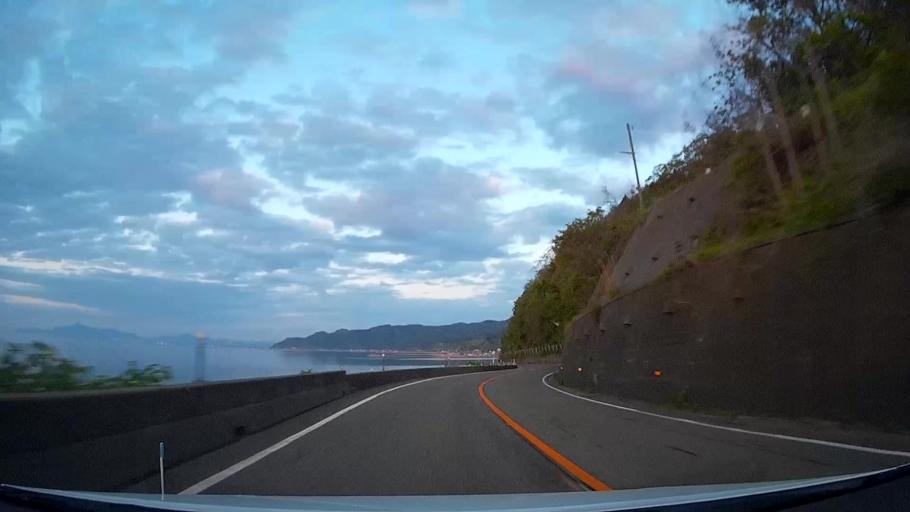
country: JP
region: Niigata
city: Joetsu
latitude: 37.1692
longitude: 138.1243
